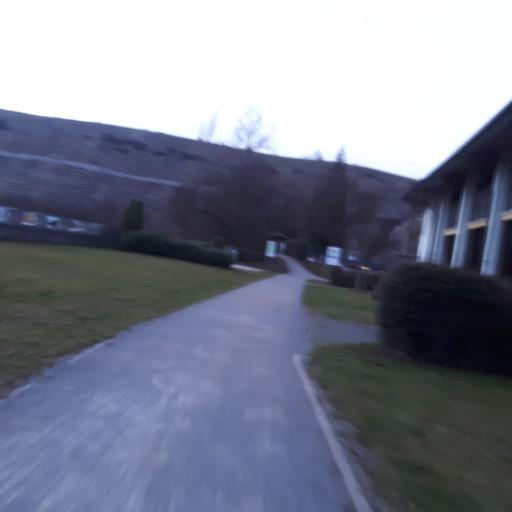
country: DE
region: Baden-Wuerttemberg
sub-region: Regierungsbezirk Stuttgart
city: Mundelsheim
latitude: 49.0008
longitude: 9.2018
